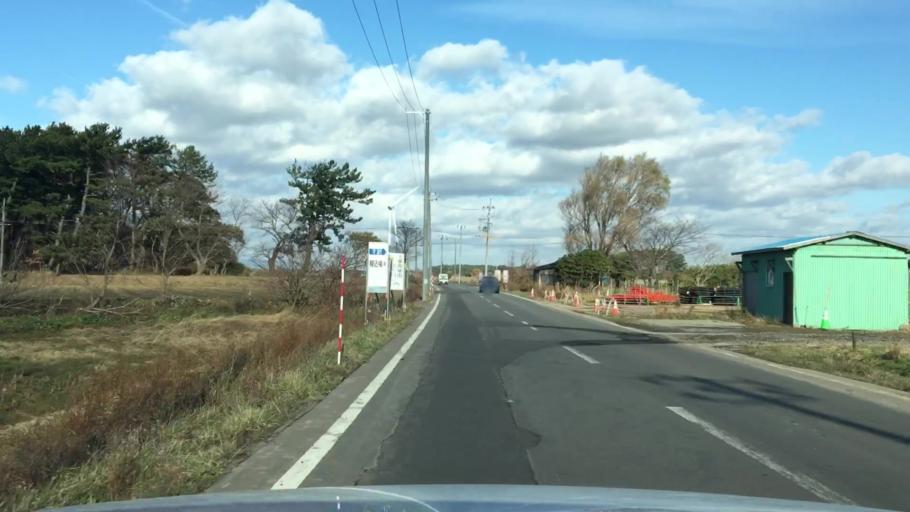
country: JP
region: Aomori
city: Shimokizukuri
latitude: 40.8552
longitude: 140.3021
